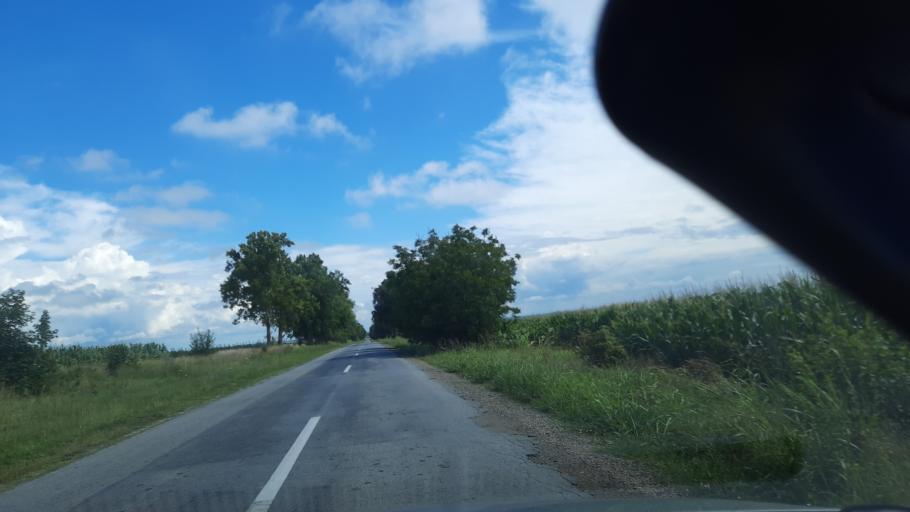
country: RS
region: Autonomna Pokrajina Vojvodina
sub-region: Sremski Okrug
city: Sremska Mitrovica
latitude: 45.0780
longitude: 19.5872
